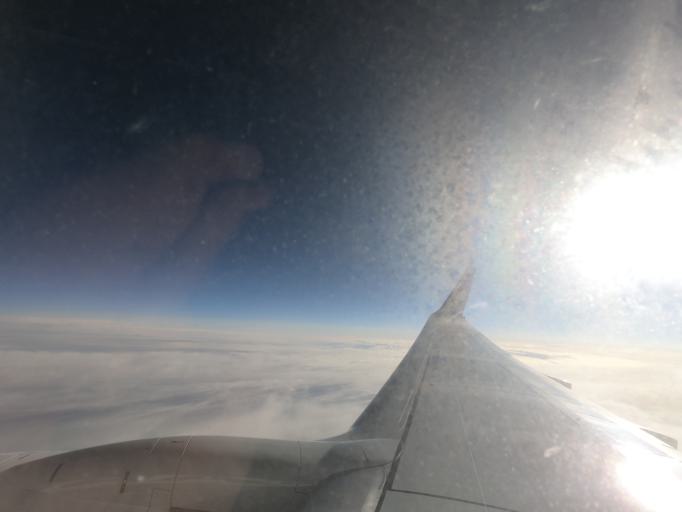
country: BE
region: Wallonia
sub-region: Province de Liege
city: Berloz
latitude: 50.7418
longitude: 5.2148
